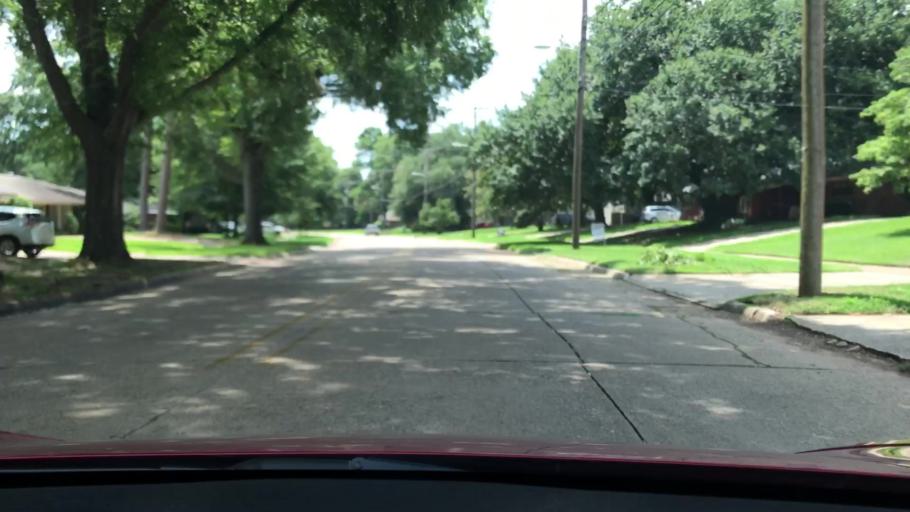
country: US
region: Louisiana
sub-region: Bossier Parish
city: Bossier City
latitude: 32.4601
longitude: -93.7346
